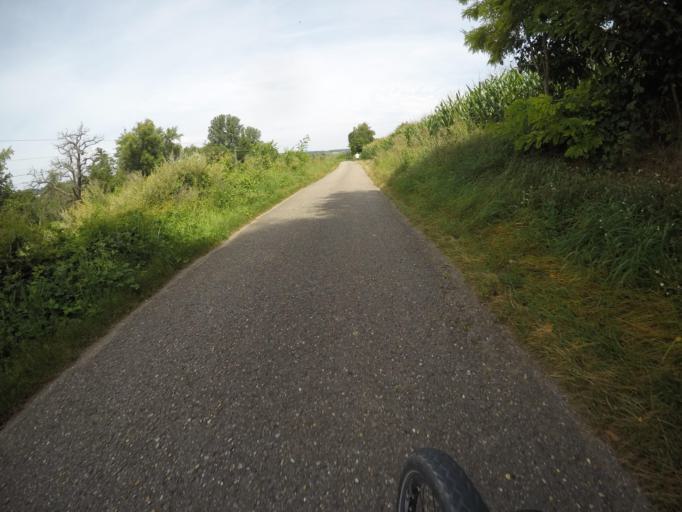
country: DE
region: Baden-Wuerttemberg
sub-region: Karlsruhe Region
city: Gondelsheim
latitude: 49.0897
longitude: 8.6512
